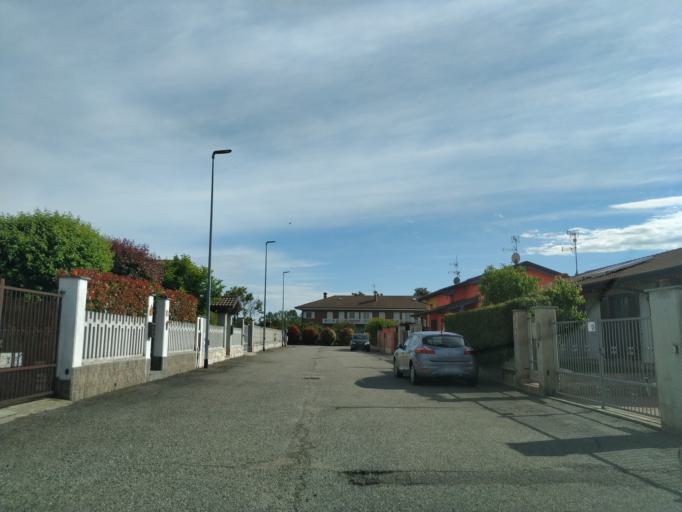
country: IT
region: Piedmont
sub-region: Provincia di Vercelli
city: Olcenengo
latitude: 45.3618
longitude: 8.3072
